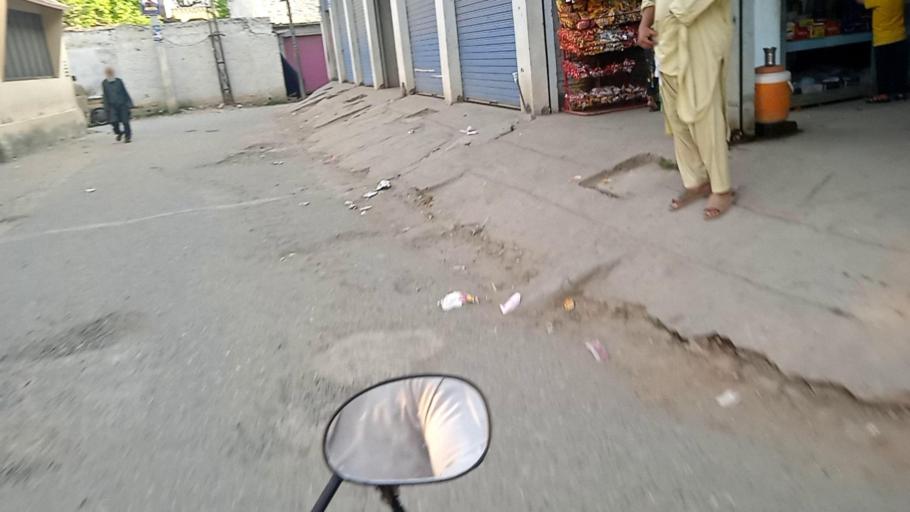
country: PK
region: Khyber Pakhtunkhwa
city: Mingora
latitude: 34.8092
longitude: 72.3612
